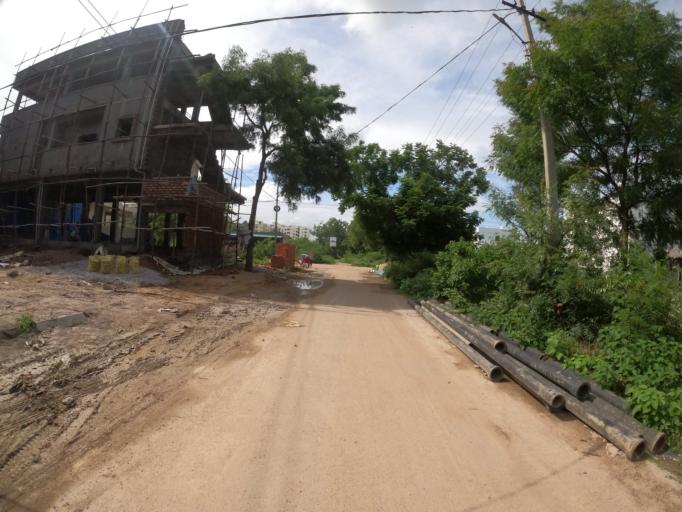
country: IN
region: Telangana
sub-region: Hyderabad
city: Hyderabad
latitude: 17.3523
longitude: 78.3981
